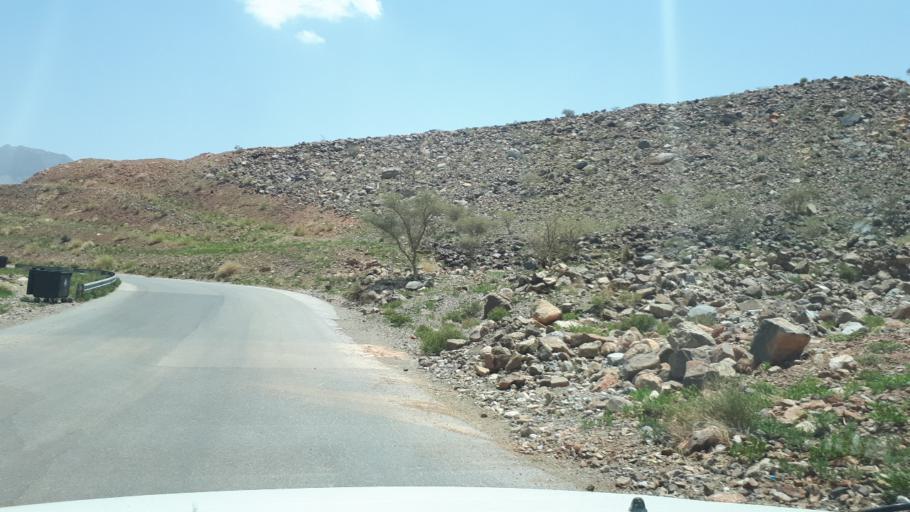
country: OM
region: Muhafazat ad Dakhiliyah
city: Bahla'
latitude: 23.1916
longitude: 57.1370
